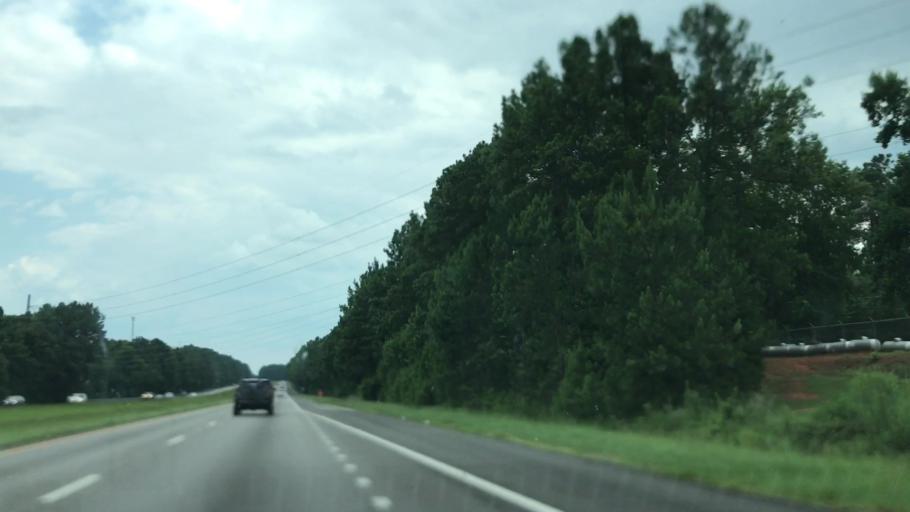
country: US
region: South Carolina
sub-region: Richland County
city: Blythewood
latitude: 34.2751
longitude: -80.9978
